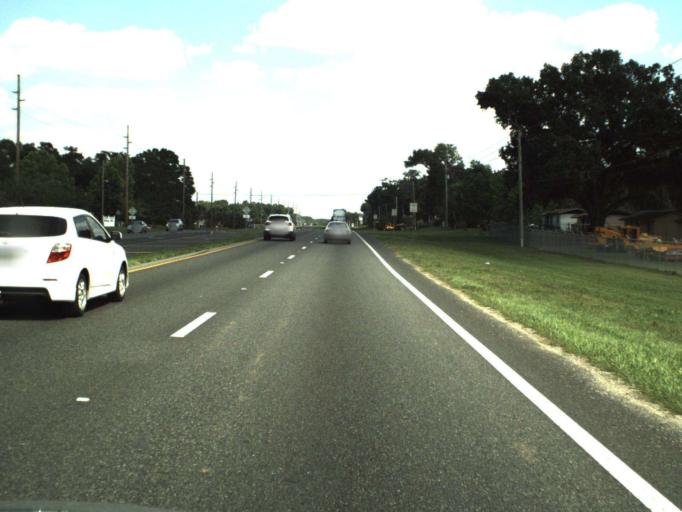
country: US
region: Florida
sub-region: Marion County
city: Ocala
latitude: 29.1546
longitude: -82.0822
